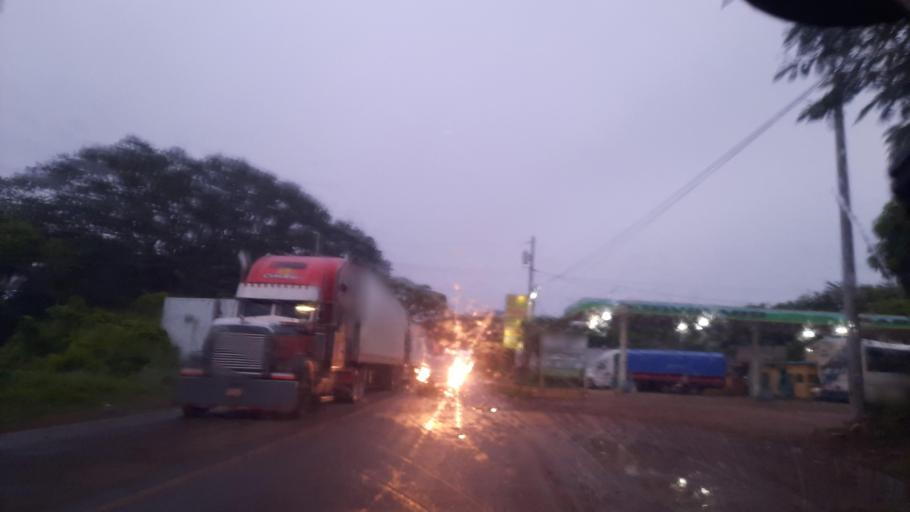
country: GT
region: Jutiapa
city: Atescatempa
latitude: 14.1978
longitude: -89.6771
